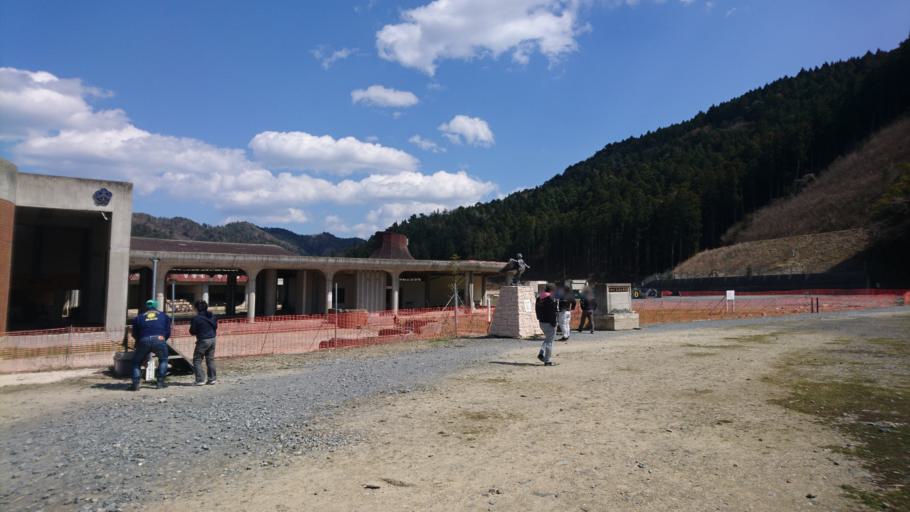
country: JP
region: Miyagi
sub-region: Oshika Gun
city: Onagawa Cho
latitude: 38.5461
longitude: 141.4277
